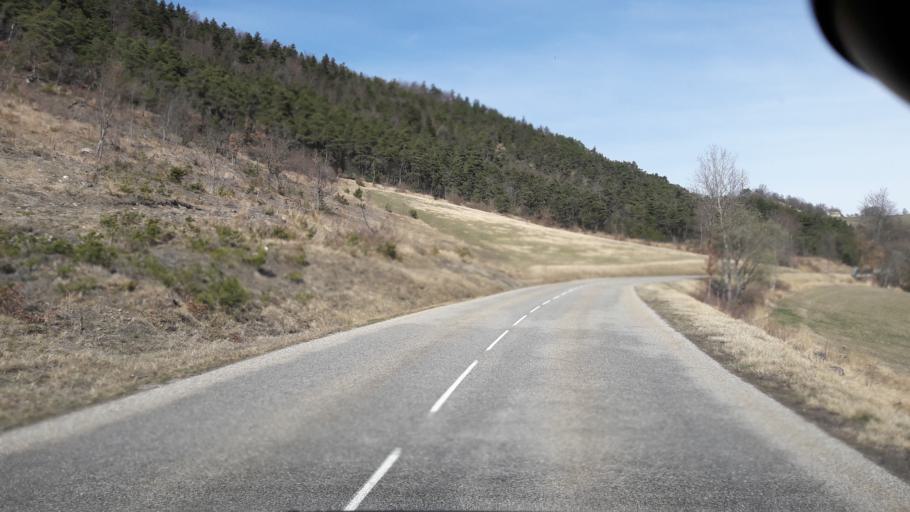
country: FR
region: Rhone-Alpes
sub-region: Departement de l'Isere
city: Mens
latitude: 44.8383
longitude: 5.7797
